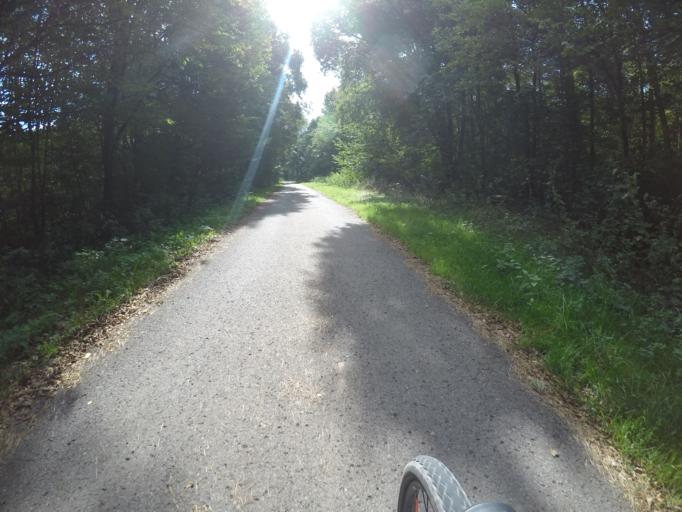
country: DE
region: Baden-Wuerttemberg
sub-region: Karlsruhe Region
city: Althengstett
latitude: 48.7165
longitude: 8.8052
